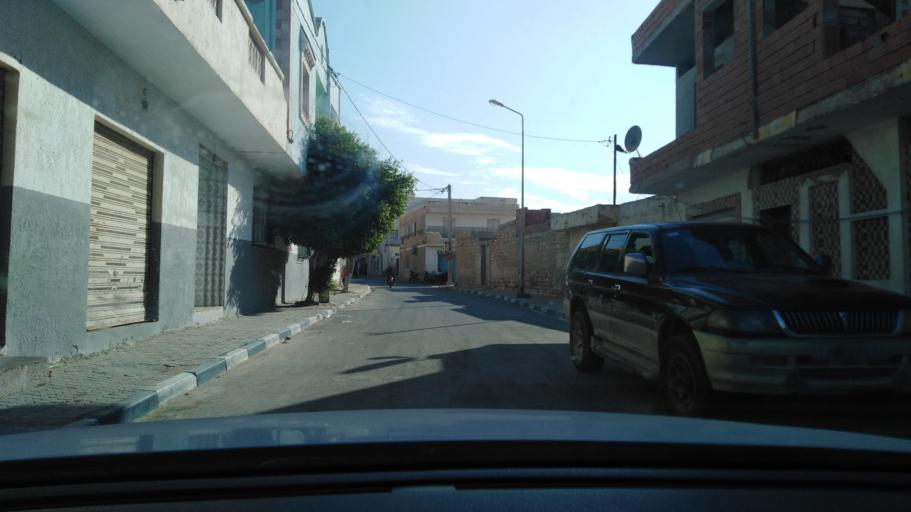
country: TN
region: Qabis
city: Gabes
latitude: 33.9381
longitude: 10.0685
